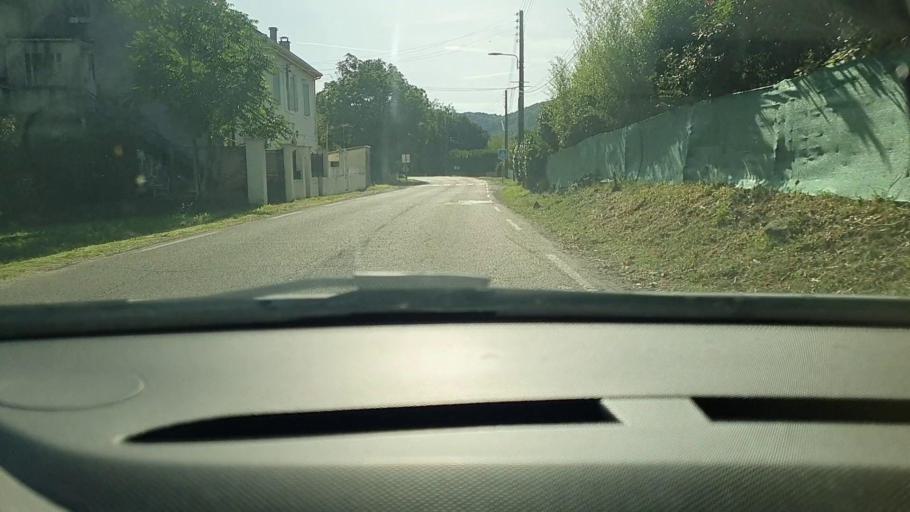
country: FR
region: Languedoc-Roussillon
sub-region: Departement du Gard
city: Saint-Florent-sur-Auzonnet
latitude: 44.2439
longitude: 4.1016
